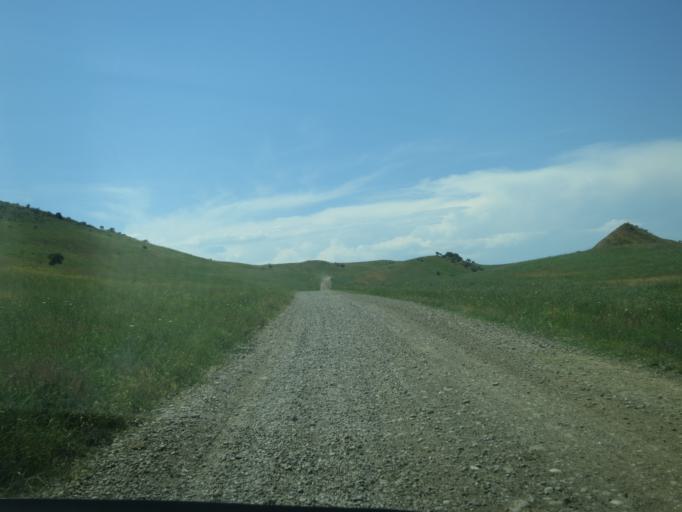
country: AZ
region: Agstafa
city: Saloglu
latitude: 41.4610
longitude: 45.3462
